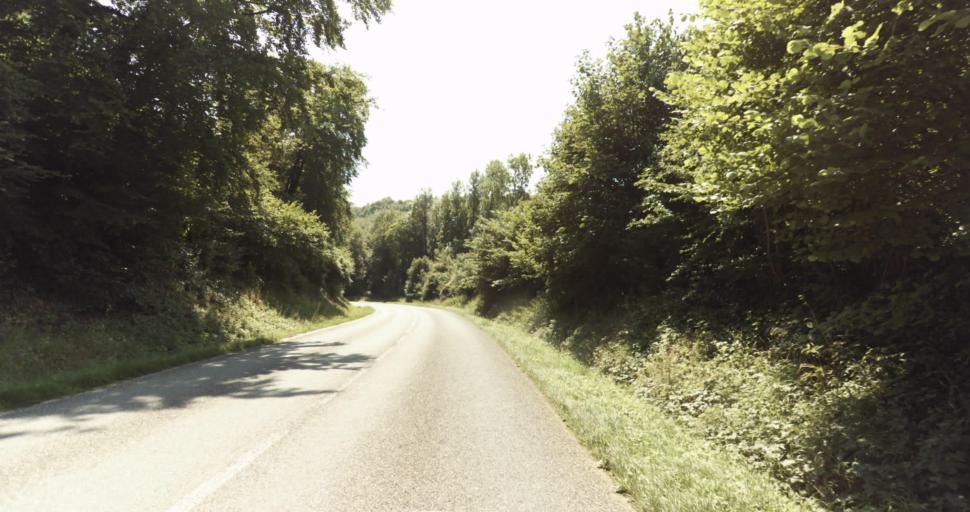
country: FR
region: Lorraine
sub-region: Departement de Meurthe-et-Moselle
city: Joeuf
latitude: 49.2444
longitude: 6.0205
